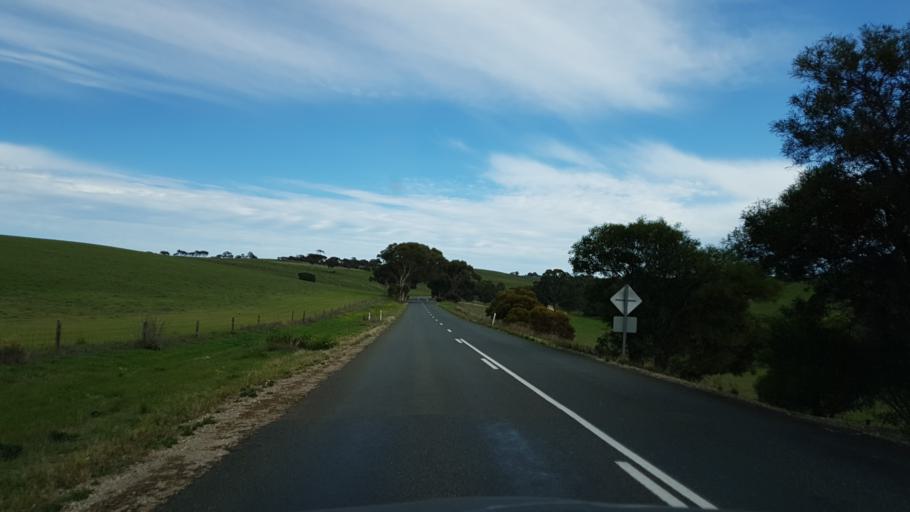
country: AU
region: South Australia
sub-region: Alexandrina
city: Strathalbyn
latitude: -35.1870
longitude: 138.9549
